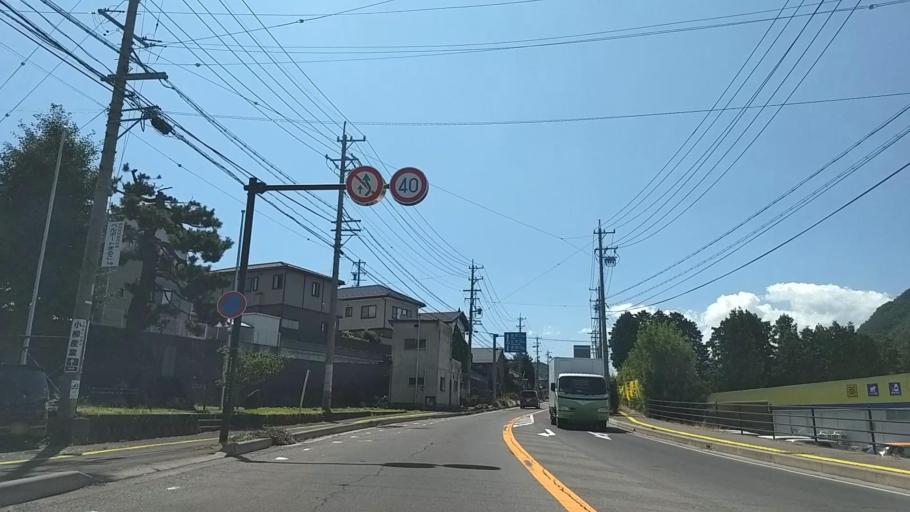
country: JP
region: Nagano
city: Kamimaruko
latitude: 36.3365
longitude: 138.2730
